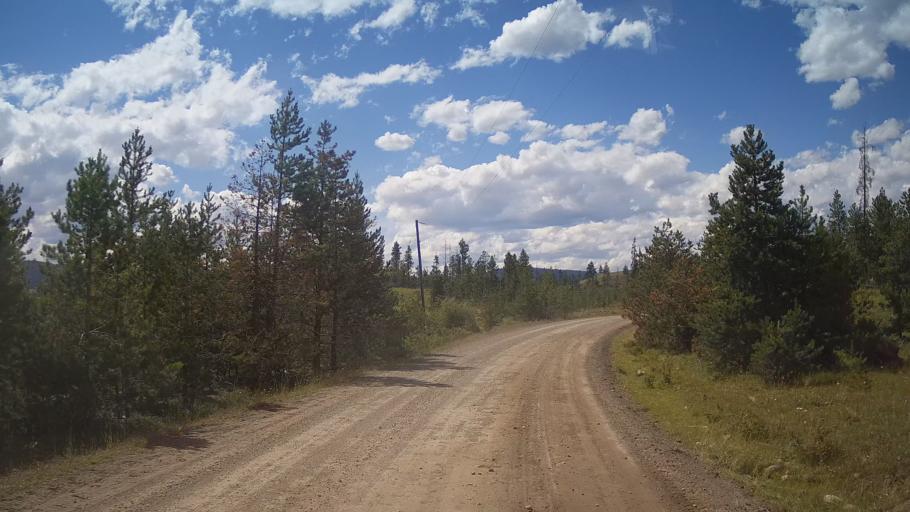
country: CA
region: British Columbia
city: Lillooet
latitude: 51.3354
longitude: -121.9681
